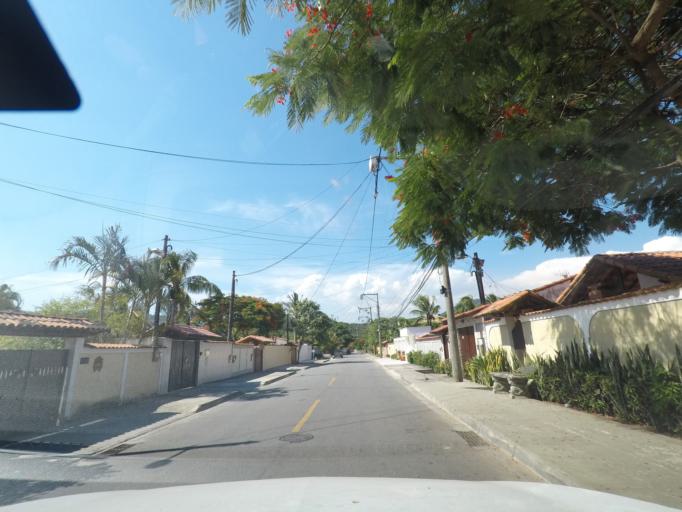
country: BR
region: Rio de Janeiro
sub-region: Niteroi
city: Niteroi
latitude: -22.9644
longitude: -42.9729
